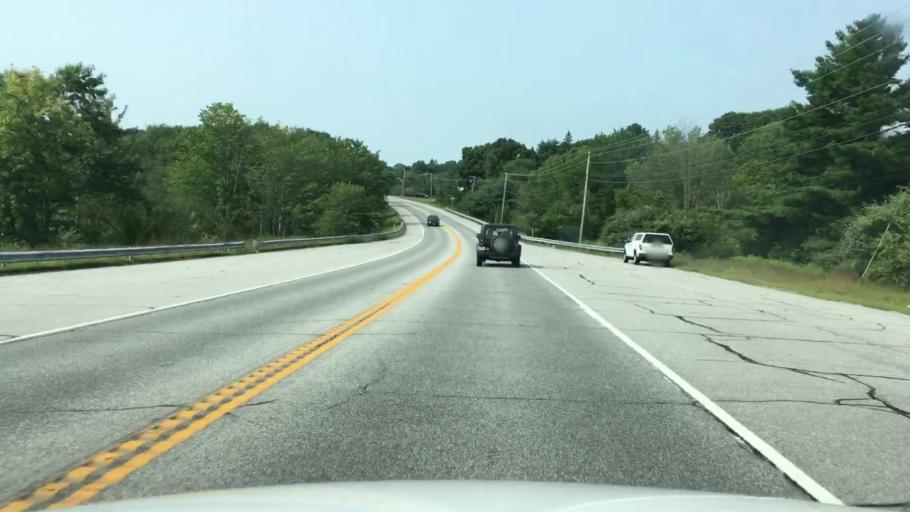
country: US
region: Maine
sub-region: Kennebec County
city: Winthrop
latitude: 44.3025
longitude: -69.9723
